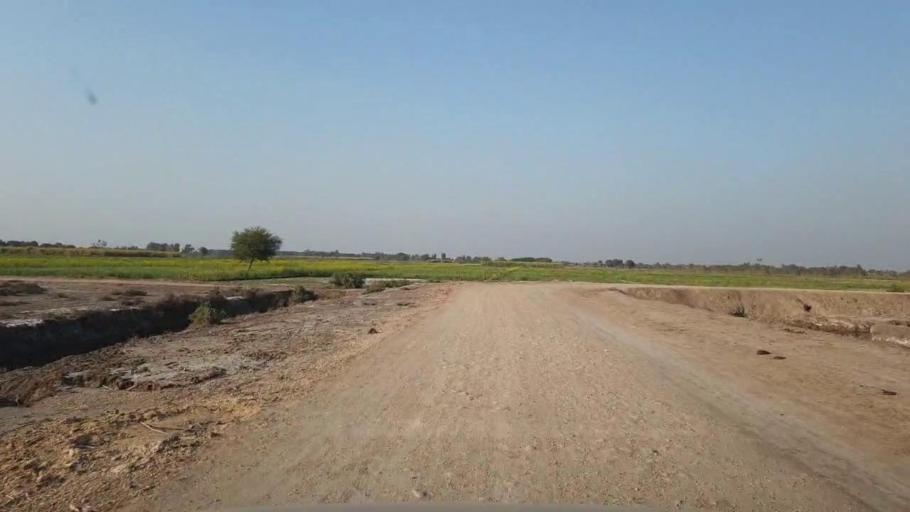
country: PK
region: Sindh
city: Chambar
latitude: 25.3403
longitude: 68.7017
